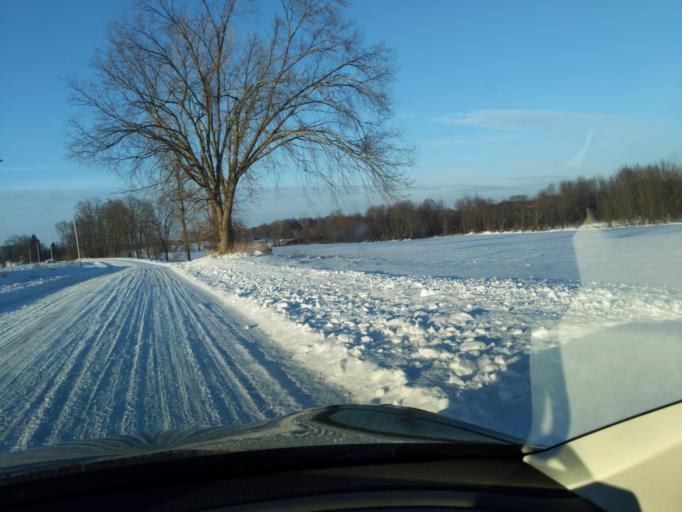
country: US
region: Michigan
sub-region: Ingham County
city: Stockbridge
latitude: 42.5006
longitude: -84.1192
